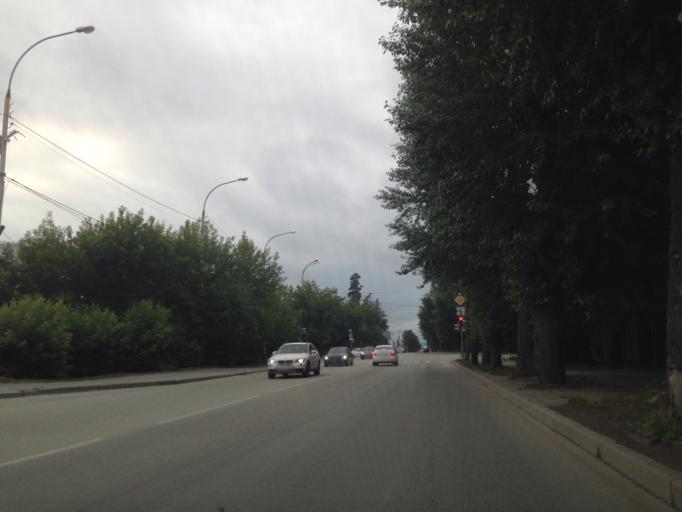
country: RU
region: Sverdlovsk
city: Yekaterinburg
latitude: 56.8340
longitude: 60.6944
